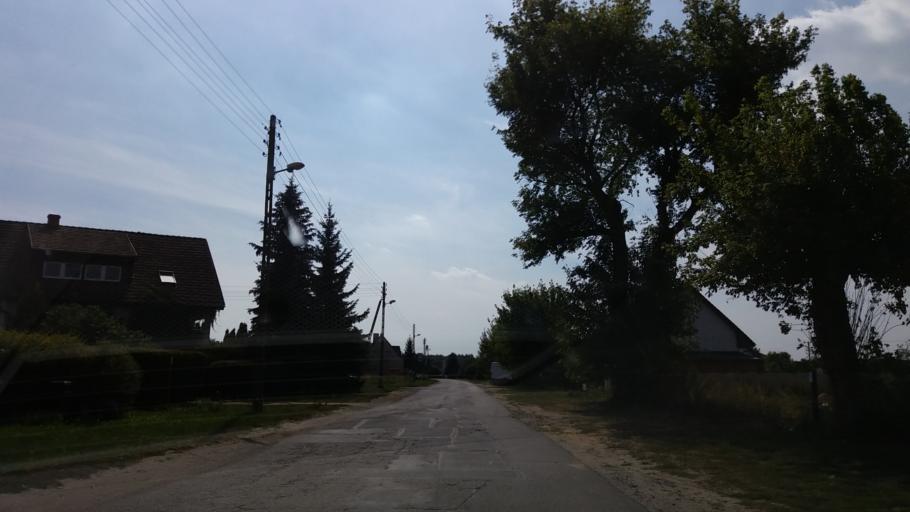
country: PL
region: West Pomeranian Voivodeship
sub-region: Powiat stargardzki
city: Stargard Szczecinski
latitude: 53.3638
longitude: 14.9718
